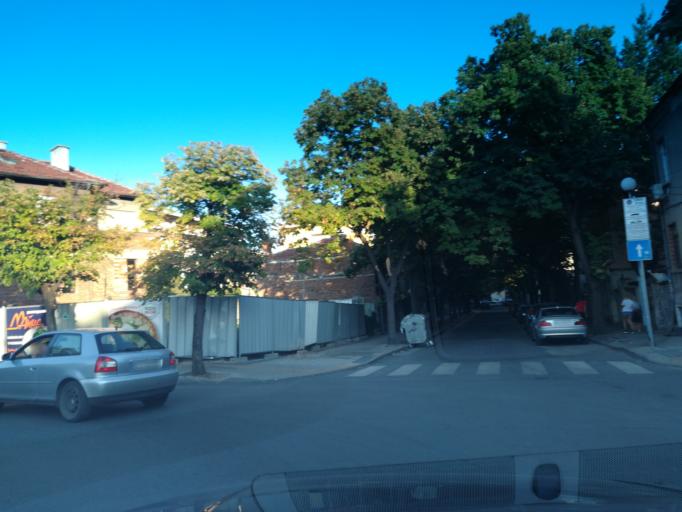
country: BG
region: Plovdiv
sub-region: Obshtina Plovdiv
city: Plovdiv
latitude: 42.1407
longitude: 24.7368
